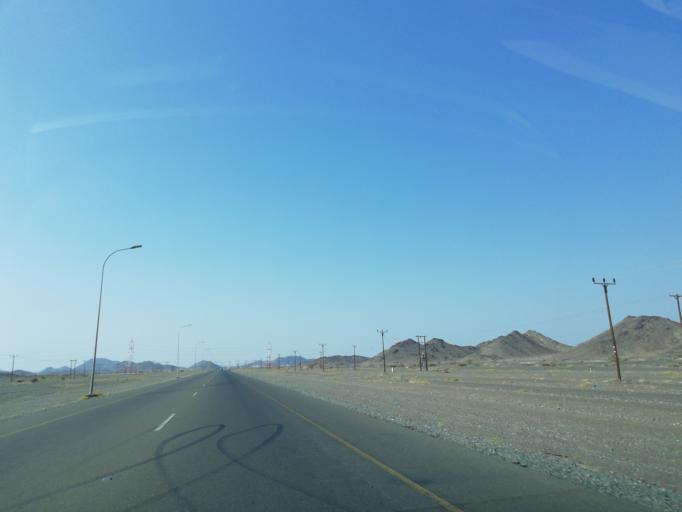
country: OM
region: Ash Sharqiyah
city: Ibra'
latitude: 22.7535
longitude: 58.1475
